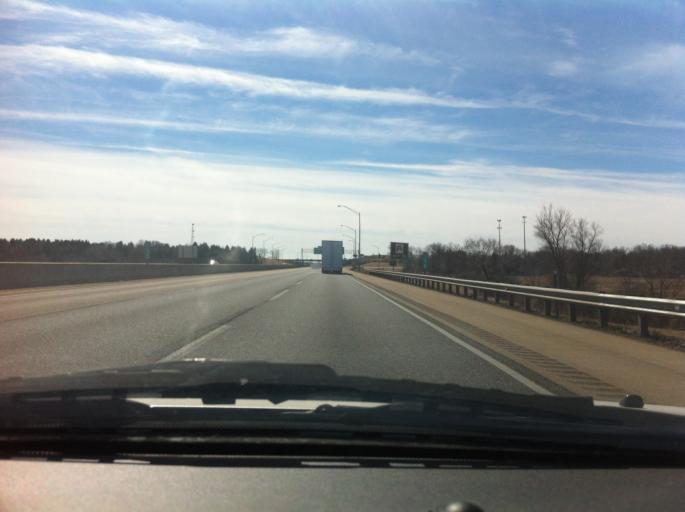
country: US
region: Illinois
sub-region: Winnebago County
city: Roscoe
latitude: 42.3805
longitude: -88.9711
